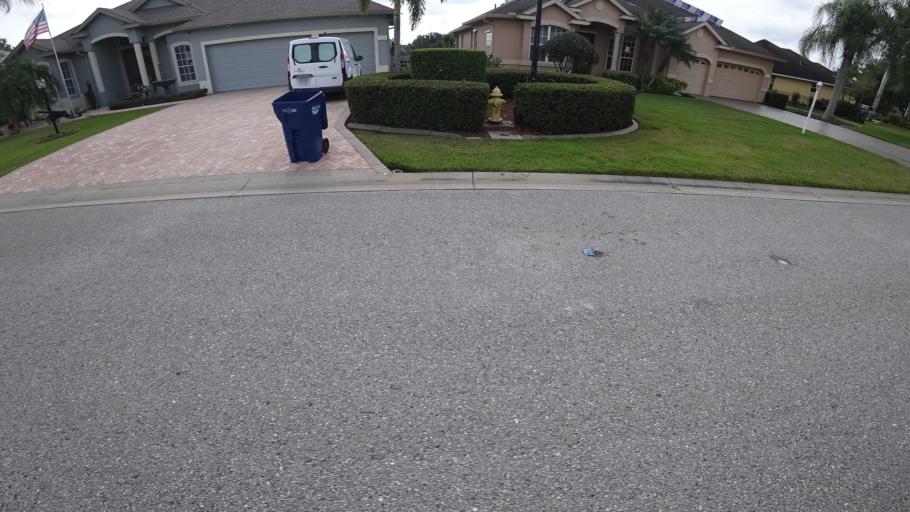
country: US
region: Florida
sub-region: Manatee County
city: Ellenton
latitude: 27.5690
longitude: -82.4740
